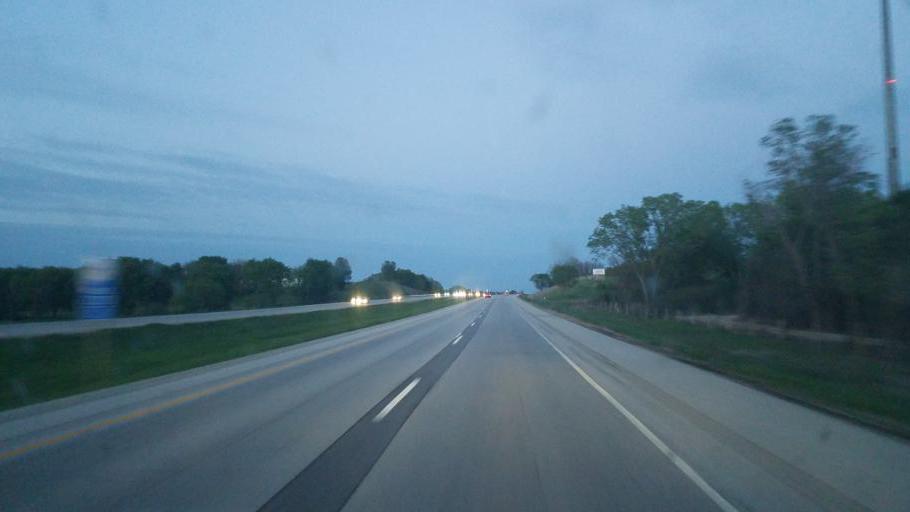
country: US
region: Wisconsin
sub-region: Jefferson County
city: Ixonia
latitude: 43.0848
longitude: -88.6465
